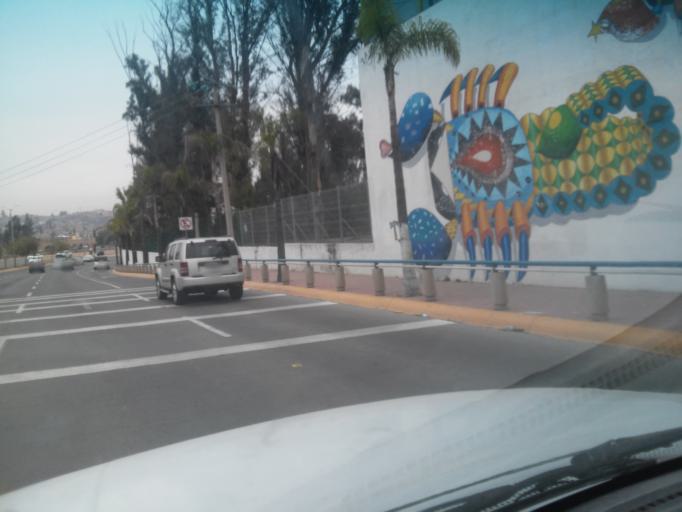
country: MX
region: Durango
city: Victoria de Durango
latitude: 24.0252
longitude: -104.6904
